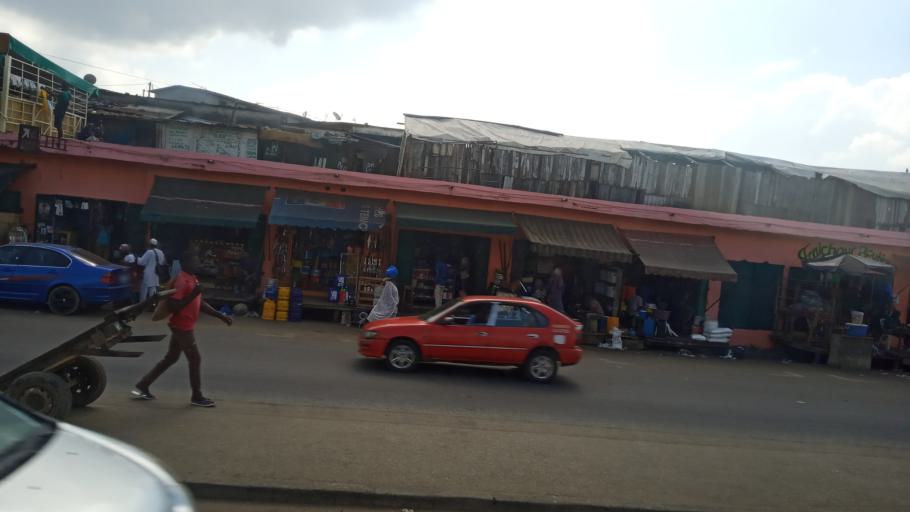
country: CI
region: Lagunes
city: Abidjan
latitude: 5.3579
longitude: -4.0305
